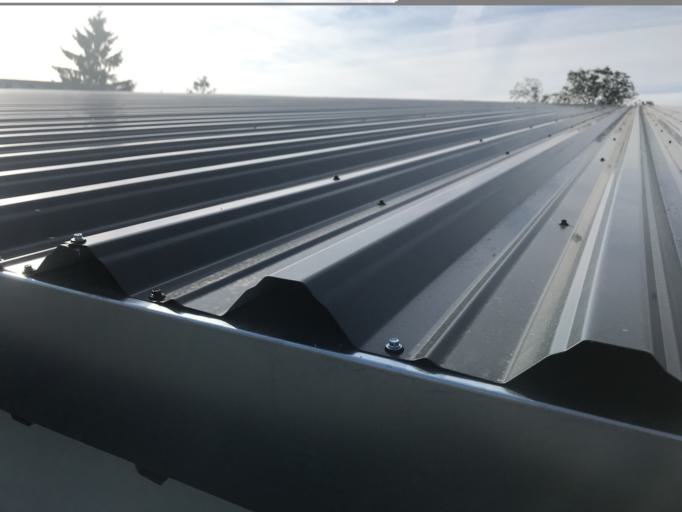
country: PL
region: Pomeranian Voivodeship
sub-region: Powiat gdanski
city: Cedry Wielkie
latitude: 54.2482
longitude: 18.8453
